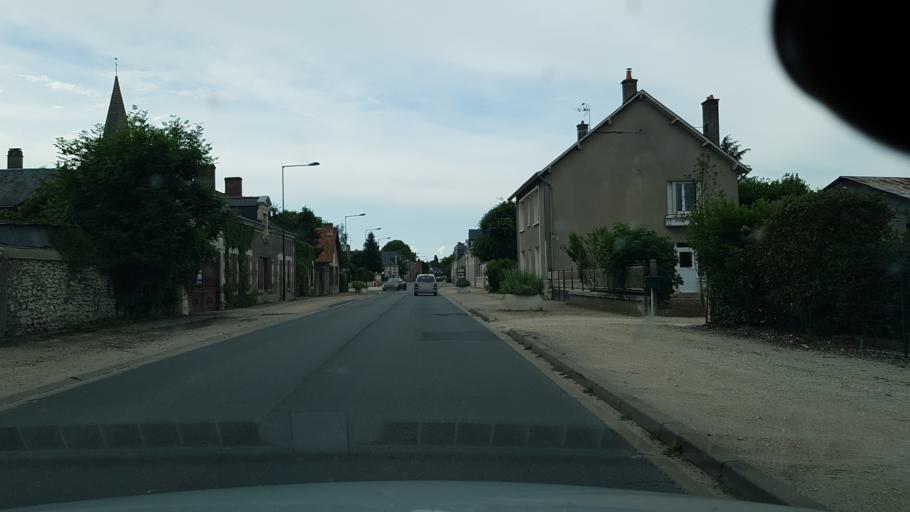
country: FR
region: Centre
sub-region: Departement du Loir-et-Cher
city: Cormeray
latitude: 47.4886
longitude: 1.4078
